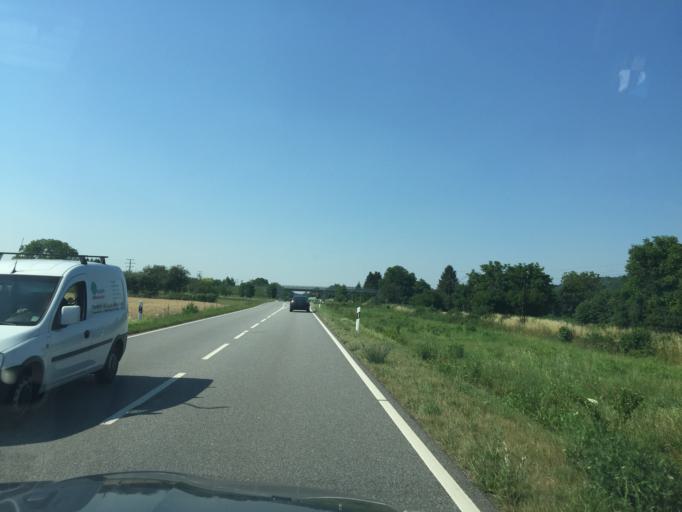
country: DE
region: Baden-Wuerttemberg
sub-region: Karlsruhe Region
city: Hemsbach
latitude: 49.5737
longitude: 8.6572
